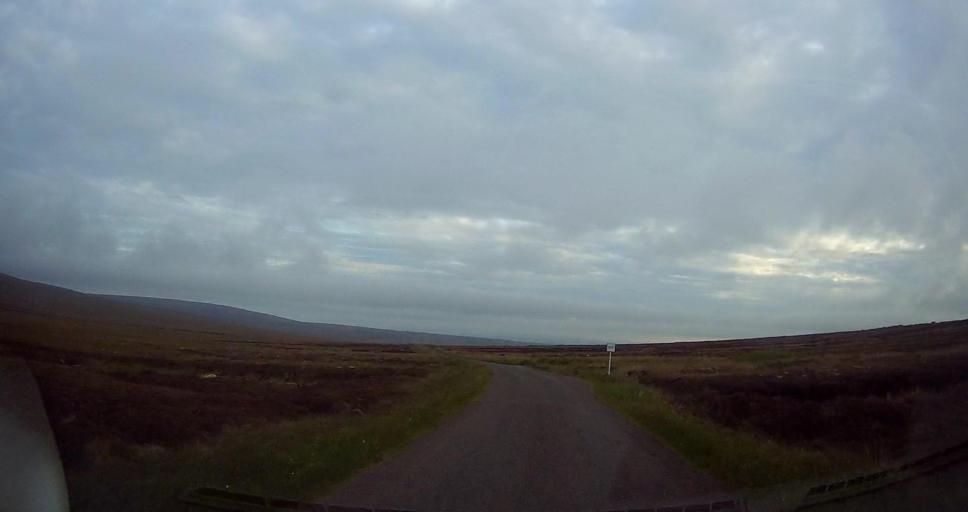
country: GB
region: Scotland
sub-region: Orkney Islands
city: Stromness
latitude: 59.1011
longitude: -3.1470
